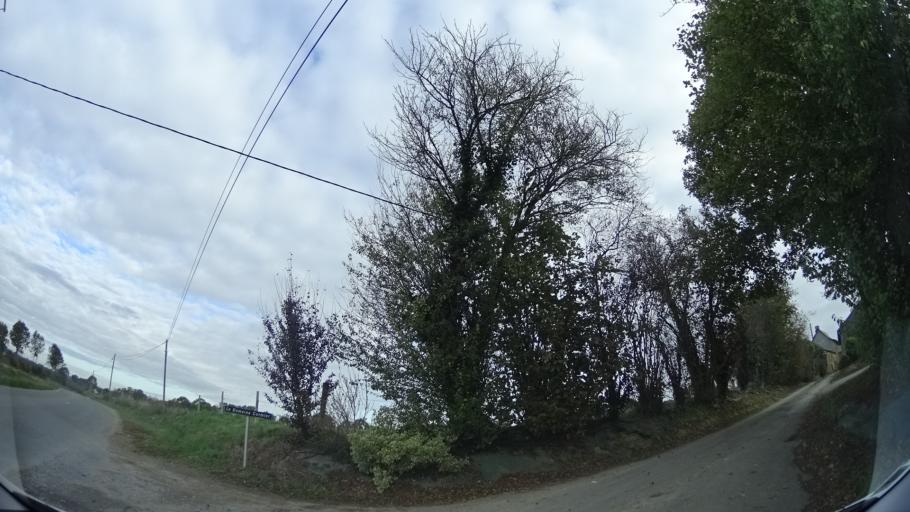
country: FR
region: Brittany
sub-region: Departement d'Ille-et-Vilaine
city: Geveze
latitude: 48.2313
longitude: -1.7867
